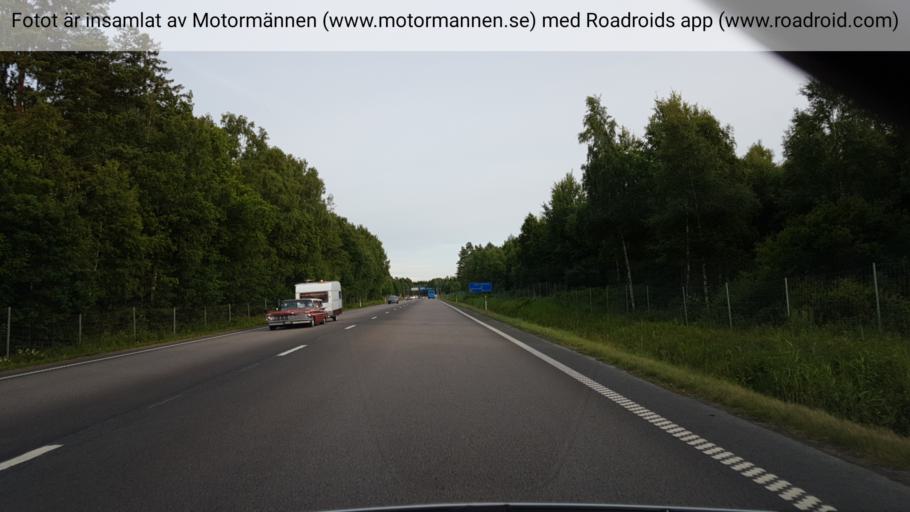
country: SE
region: Vaestra Goetaland
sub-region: Lidkopings Kommun
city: Vinninga
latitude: 58.4557
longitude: 13.2353
